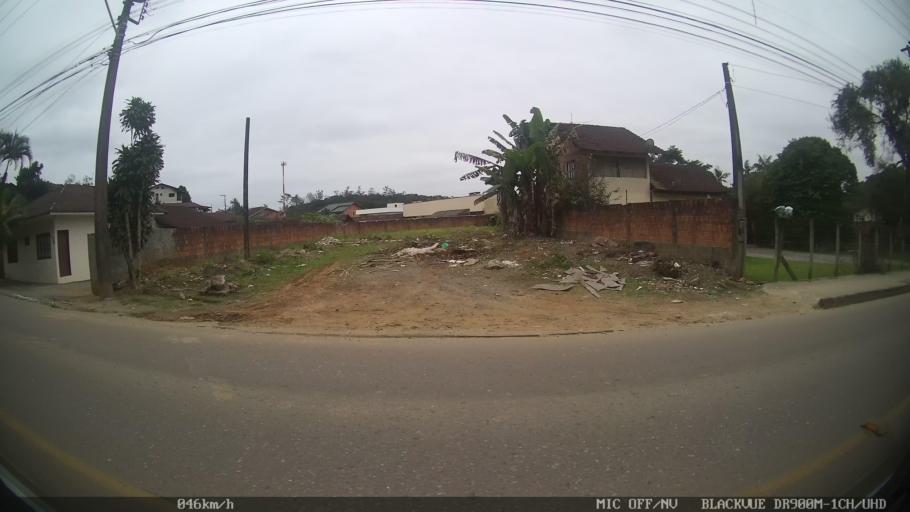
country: BR
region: Santa Catarina
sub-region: Joinville
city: Joinville
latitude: -26.3601
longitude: -48.8464
